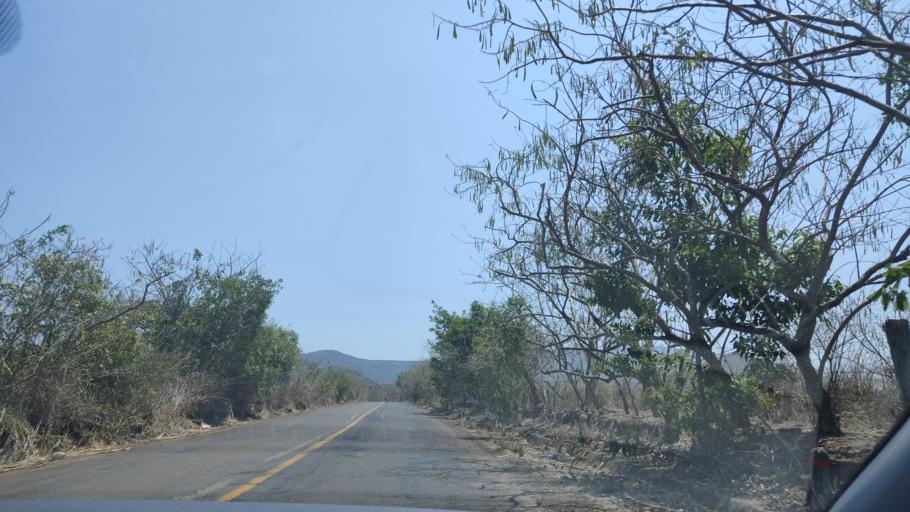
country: MX
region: Nayarit
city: Puga
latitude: 21.5800
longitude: -104.7737
